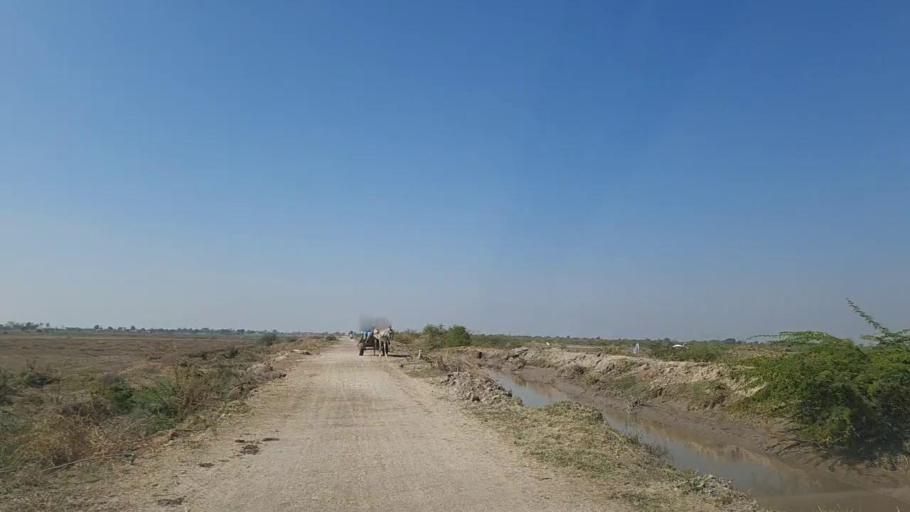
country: PK
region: Sindh
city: Pithoro
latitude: 25.4283
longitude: 69.3552
